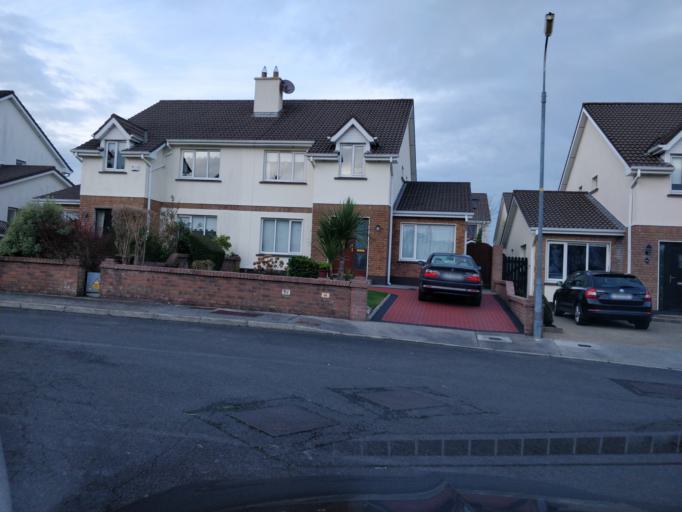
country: IE
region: Connaught
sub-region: County Galway
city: Bearna
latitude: 53.2679
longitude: -9.1096
